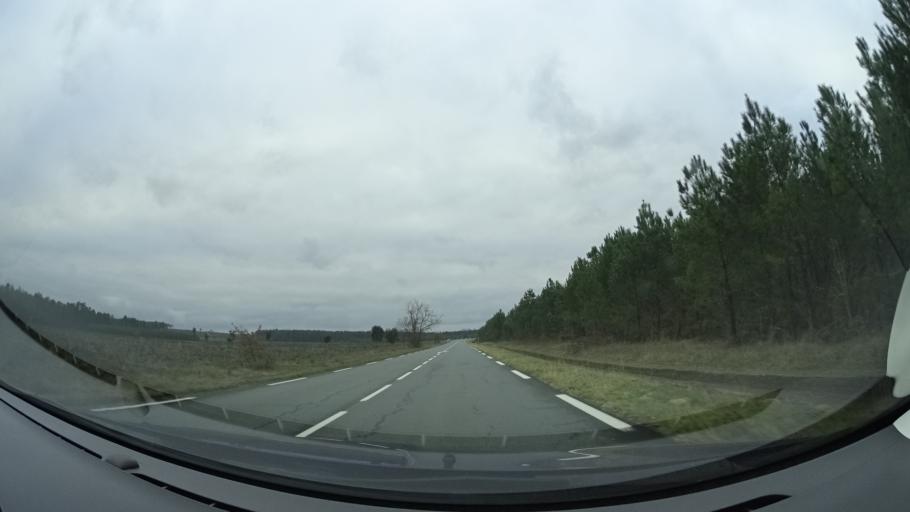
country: FR
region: Aquitaine
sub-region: Departement du Lot-et-Garonne
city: Buzet-sur-Baise
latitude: 44.2256
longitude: 0.2216
